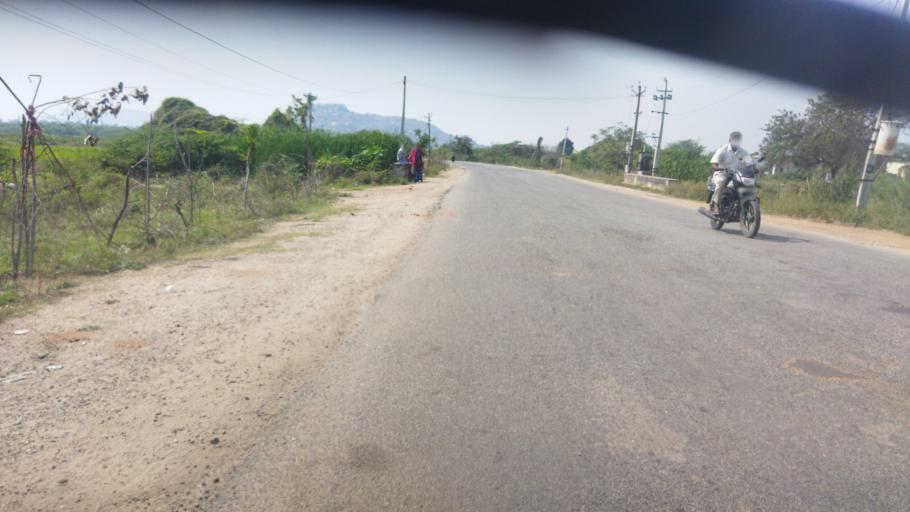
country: IN
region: Telangana
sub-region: Nalgonda
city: Nalgonda
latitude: 17.1181
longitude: 79.2846
